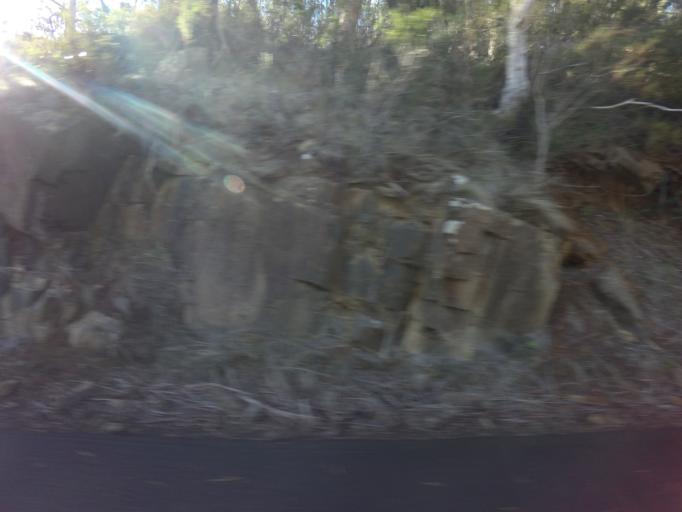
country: AU
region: Tasmania
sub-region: Glenorchy
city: Berriedale
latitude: -42.8206
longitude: 147.1799
